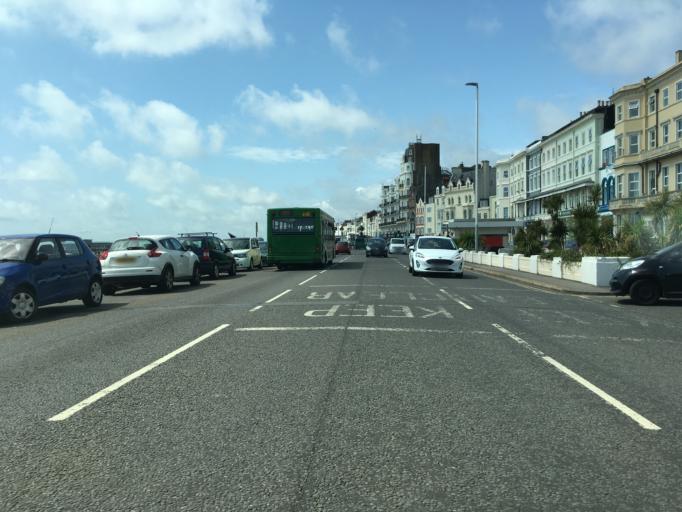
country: GB
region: England
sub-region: East Sussex
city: Hastings
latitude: 50.8545
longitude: 0.5781
